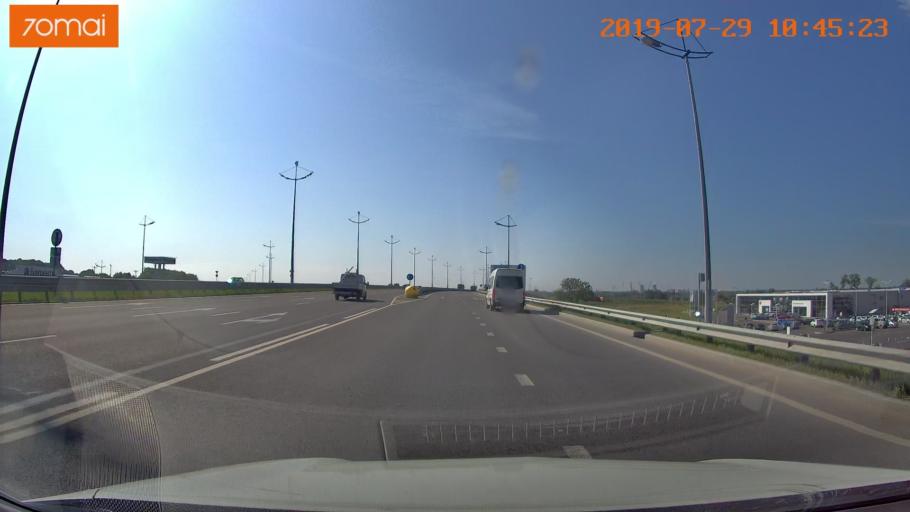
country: RU
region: Kaliningrad
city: Bol'shoe Isakovo
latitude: 54.7085
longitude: 20.5977
